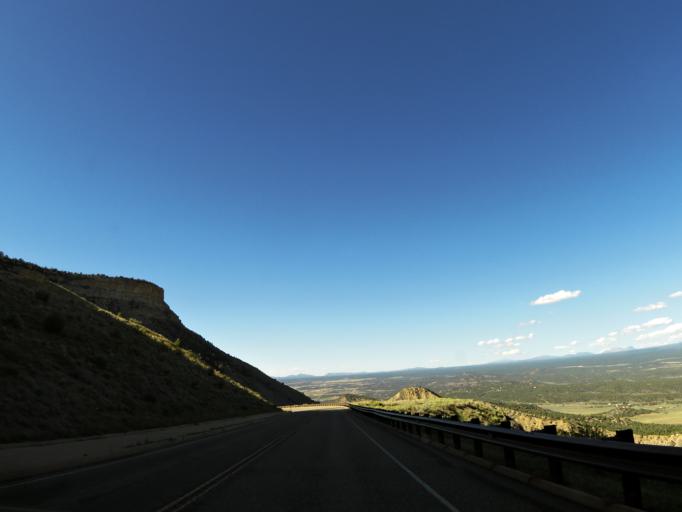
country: US
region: Colorado
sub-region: Montezuma County
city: Mancos
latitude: 37.3072
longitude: -108.4129
